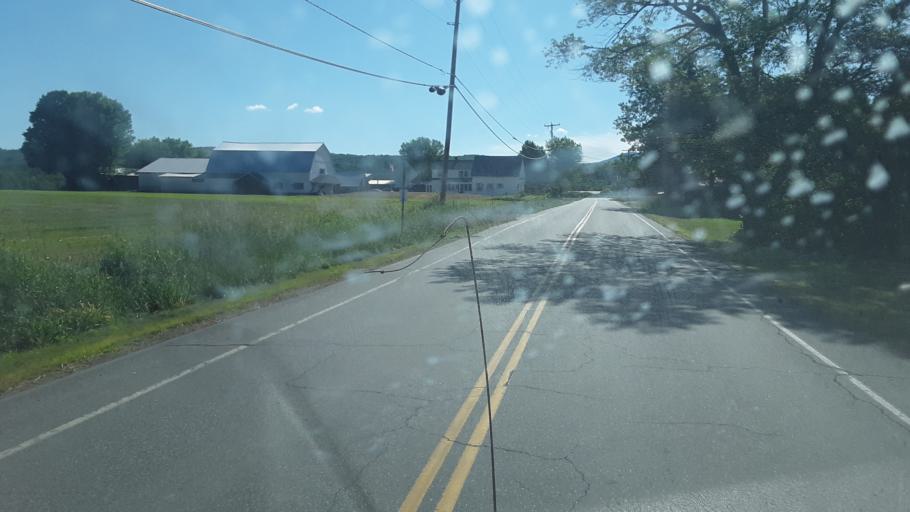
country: US
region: New Hampshire
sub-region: Grafton County
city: North Haverhill
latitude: 44.0860
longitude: -72.0173
